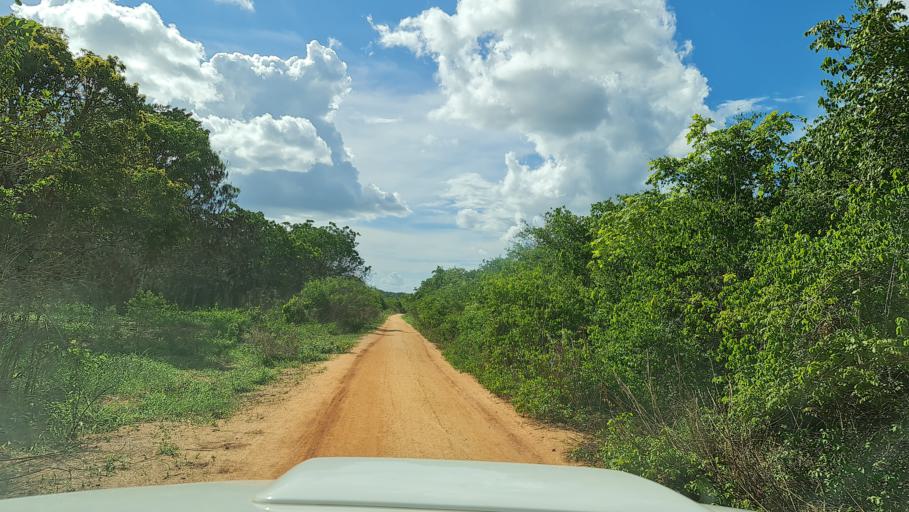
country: MZ
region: Nampula
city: Ilha de Mocambique
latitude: -15.4114
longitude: 40.2504
